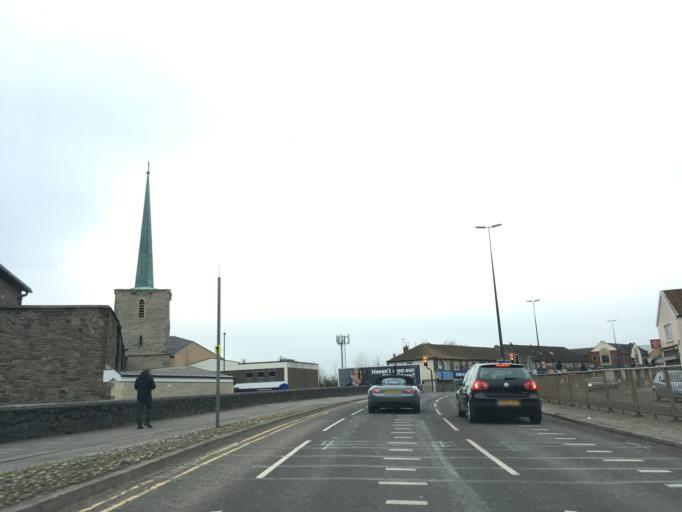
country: GB
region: England
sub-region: South Gloucestershire
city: Stoke Gifford
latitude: 51.5106
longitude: -2.5737
